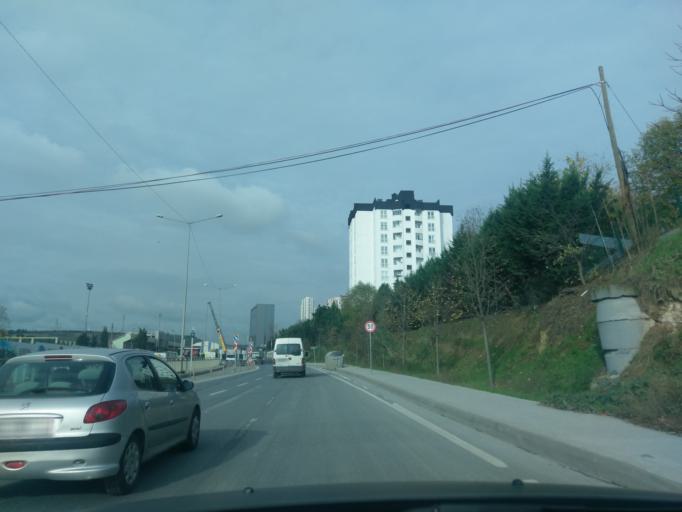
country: TR
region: Istanbul
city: Basaksehir
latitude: 41.0543
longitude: 28.7750
